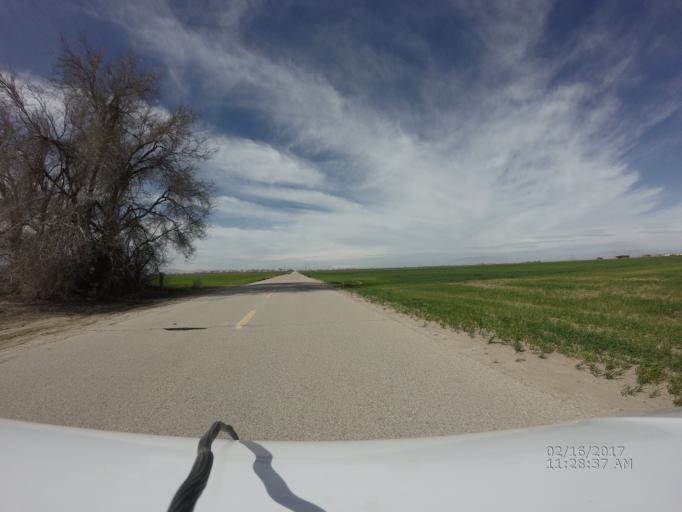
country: US
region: California
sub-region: Los Angeles County
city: Lake Los Angeles
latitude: 34.7048
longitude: -117.9207
